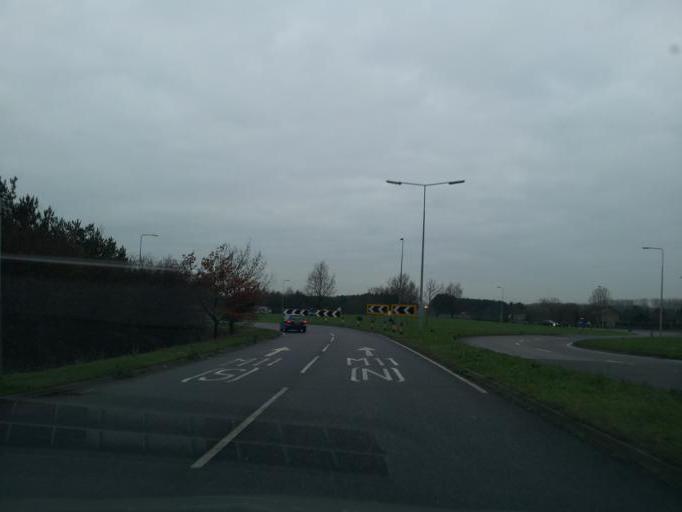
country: GB
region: England
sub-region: Cambridgeshire
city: Grantchester
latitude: 52.1921
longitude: 0.0792
